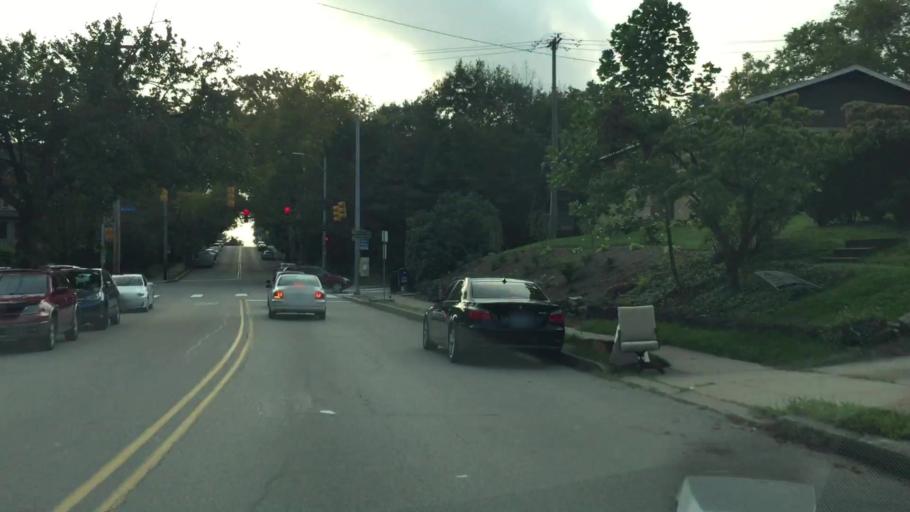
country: US
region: Pennsylvania
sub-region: Allegheny County
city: Bloomfield
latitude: 40.4381
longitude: -79.9270
